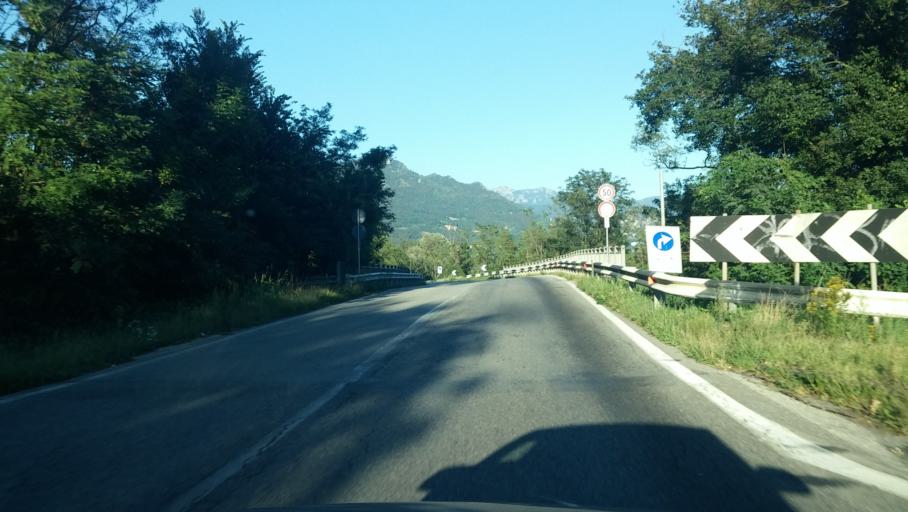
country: IT
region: Lombardy
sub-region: Provincia di Lecco
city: Suello
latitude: 45.8199
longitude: 9.3221
